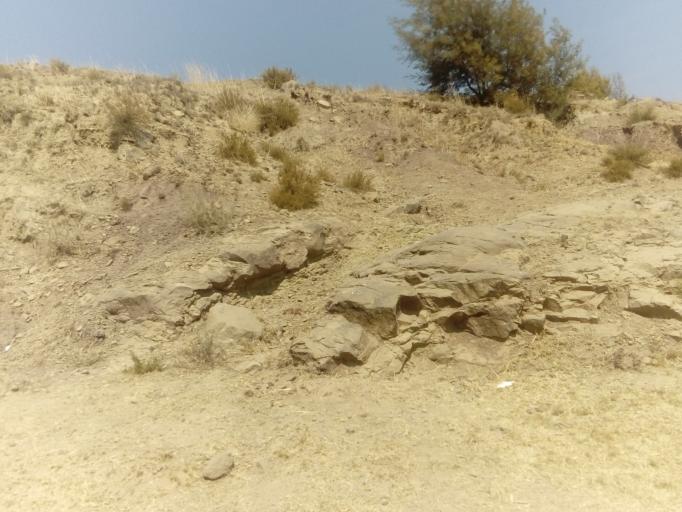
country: LS
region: Leribe
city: Leribe
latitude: -29.1343
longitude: 28.0673
